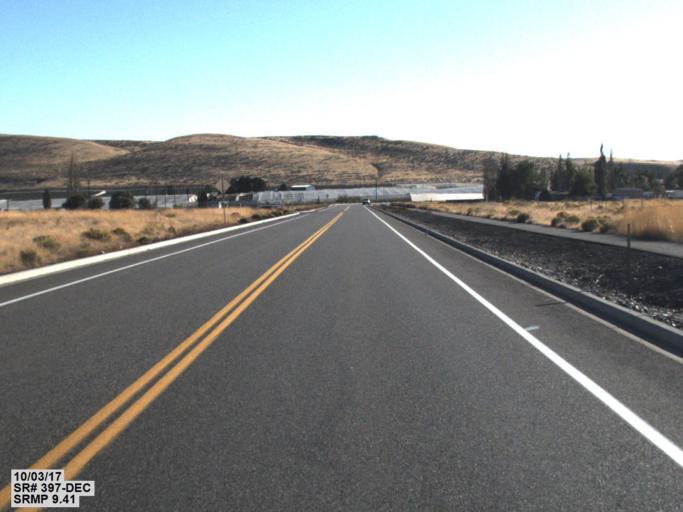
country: US
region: Washington
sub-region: Benton County
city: Finley
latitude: 46.1356
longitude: -119.0348
